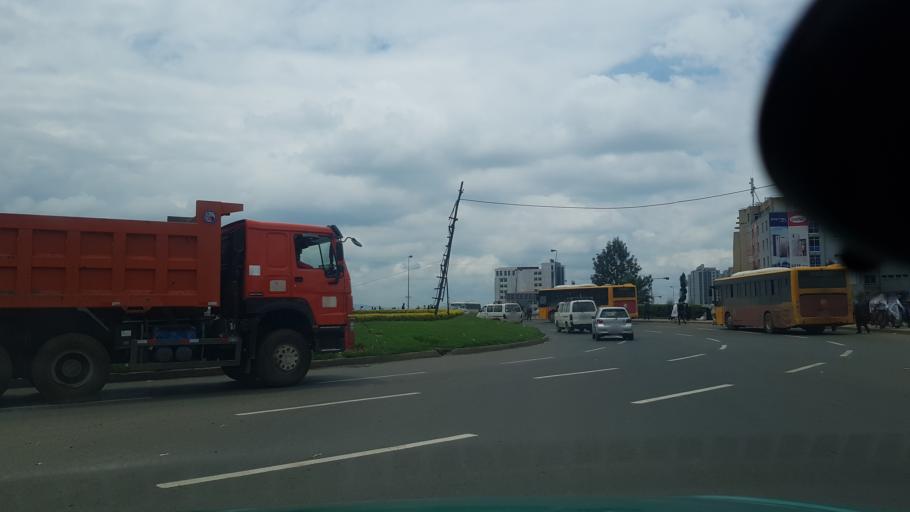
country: ET
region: Adis Abeba
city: Addis Ababa
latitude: 9.0216
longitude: 38.8010
